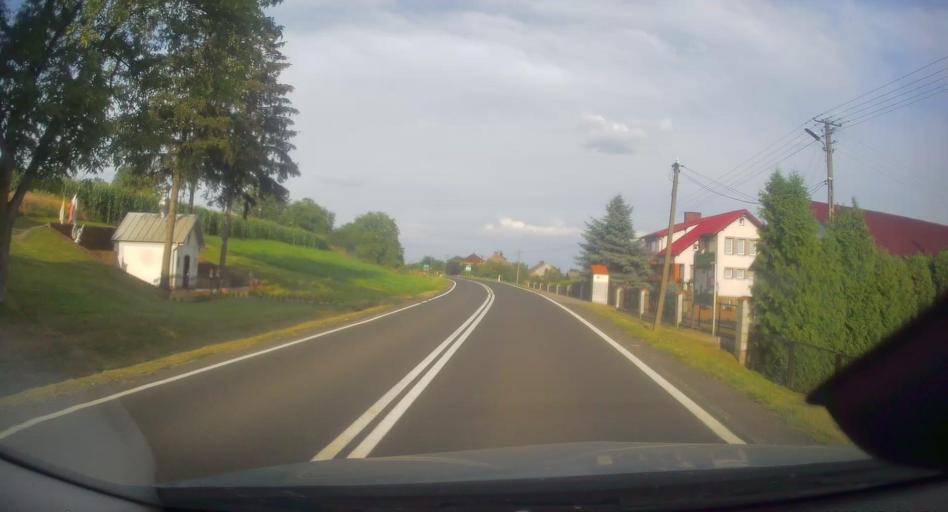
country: PL
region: Lesser Poland Voivodeship
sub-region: Powiat bochenski
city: Dziewin
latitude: 50.1428
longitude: 20.4851
